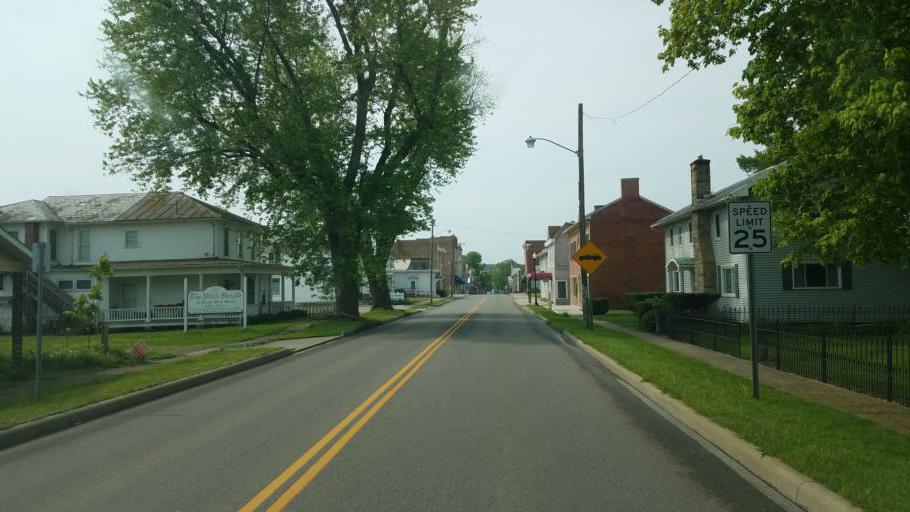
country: US
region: Ohio
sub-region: Licking County
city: Utica
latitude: 40.2358
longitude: -82.4526
